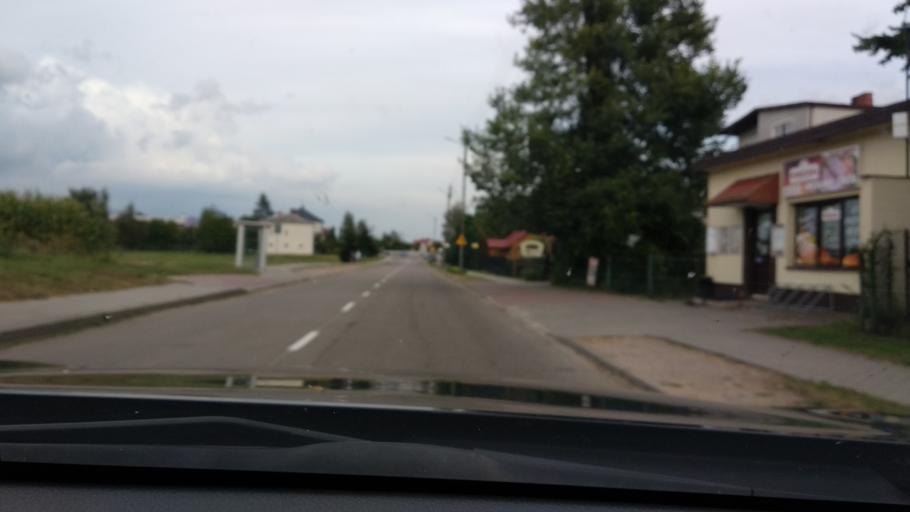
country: PL
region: Masovian Voivodeship
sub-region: Powiat pultuski
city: Obryte
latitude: 52.7164
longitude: 21.2563
